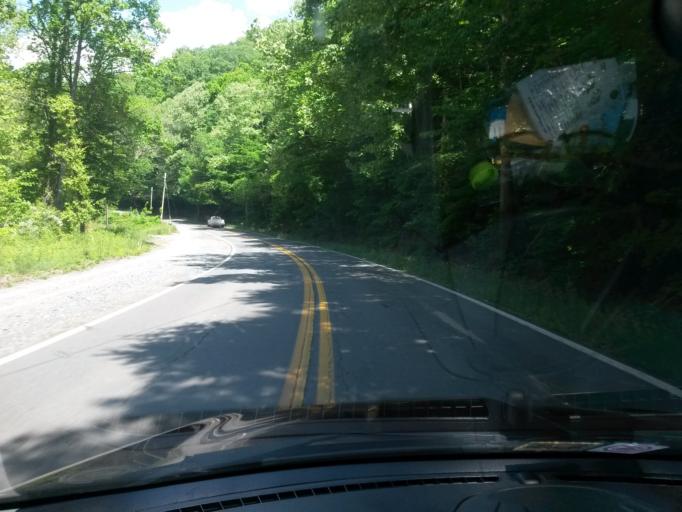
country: US
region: West Virginia
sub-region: Wyoming County
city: Pineville
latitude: 37.5255
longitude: -81.5901
